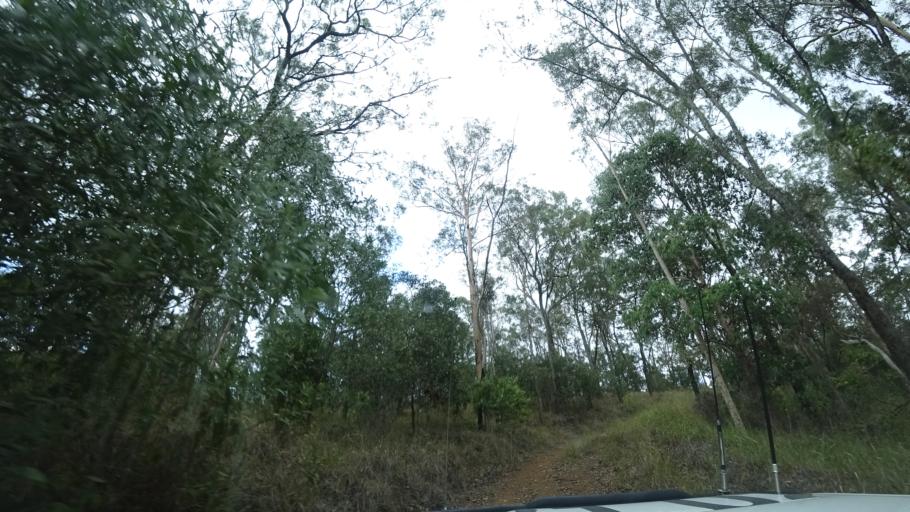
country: AU
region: Queensland
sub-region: Brisbane
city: Pullenvale
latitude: -27.4635
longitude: 152.8622
